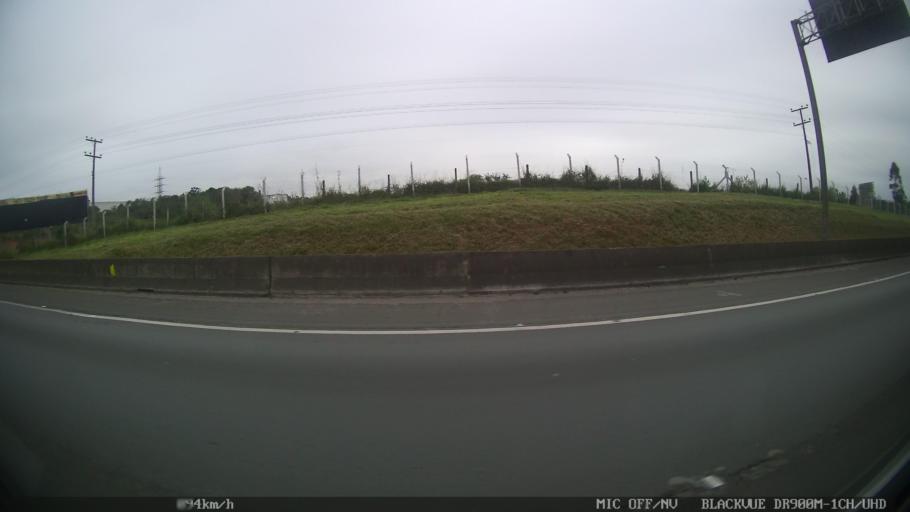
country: BR
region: Santa Catarina
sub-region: Penha
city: Penha
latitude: -26.7551
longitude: -48.6898
